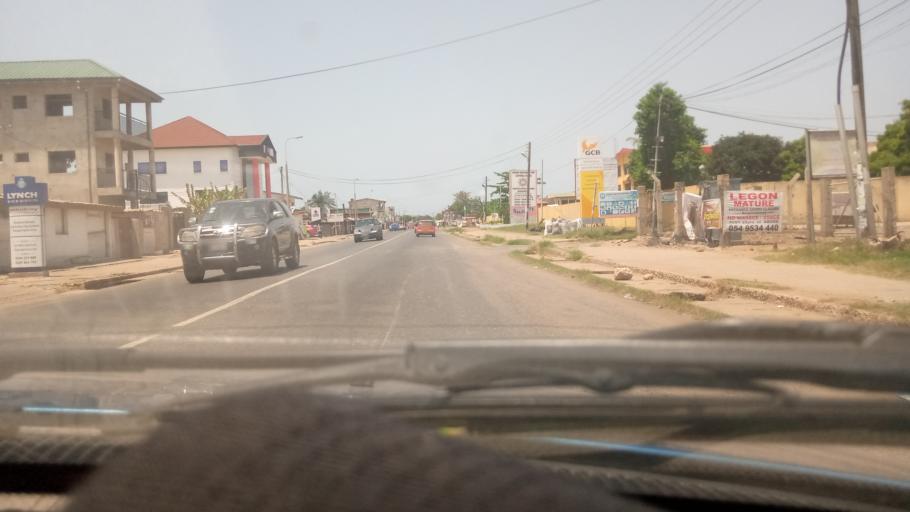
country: GH
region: Greater Accra
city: Accra
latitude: 5.5351
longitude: -0.2316
